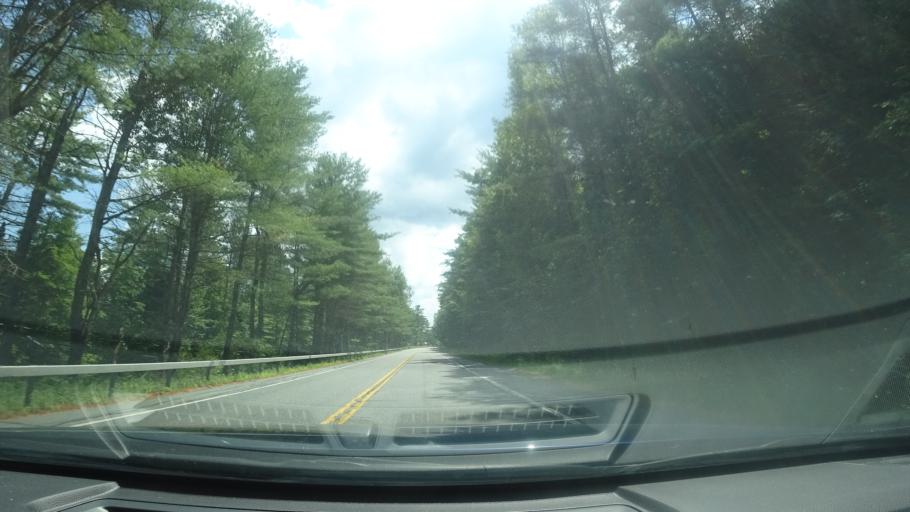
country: US
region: New York
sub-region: Warren County
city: Warrensburg
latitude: 43.5300
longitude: -73.7924
